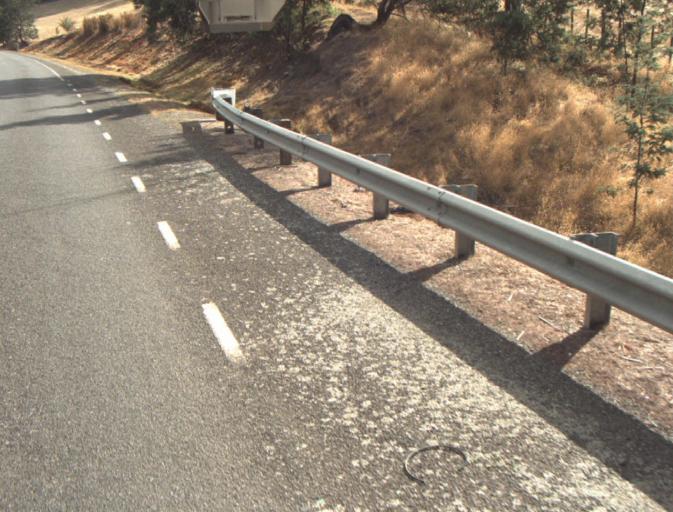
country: AU
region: Tasmania
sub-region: Launceston
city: Mayfield
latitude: -41.2919
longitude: 147.2162
